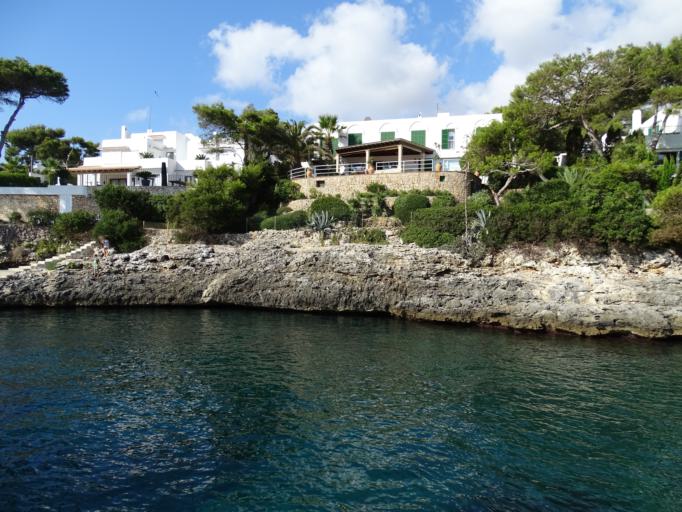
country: ES
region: Balearic Islands
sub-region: Illes Balears
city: Santanyi
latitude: 39.3715
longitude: 3.2333
